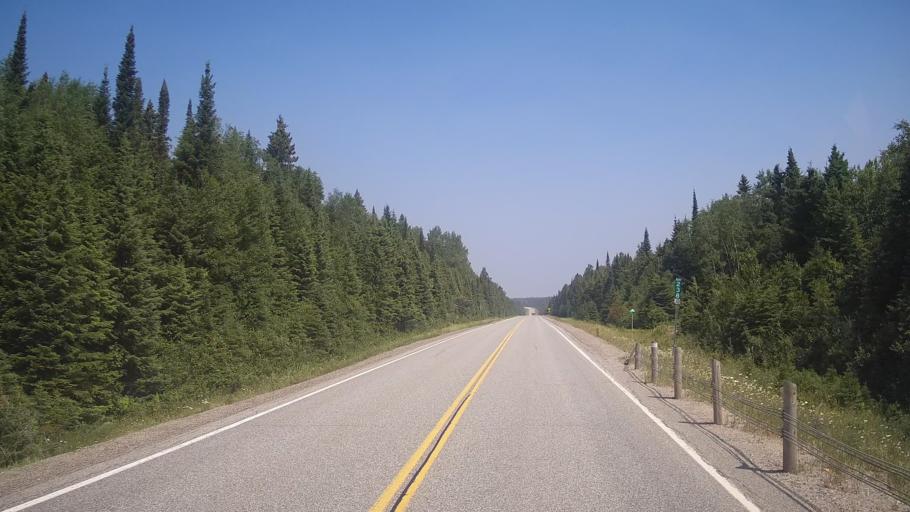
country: CA
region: Ontario
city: Timmins
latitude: 48.0855
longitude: -81.5961
